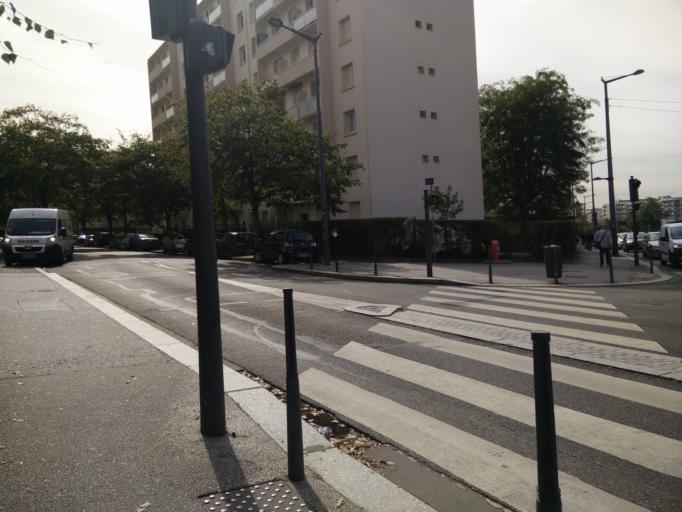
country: FR
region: Rhone-Alpes
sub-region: Departement du Rhone
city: Villeurbanne
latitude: 45.7409
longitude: 4.8757
